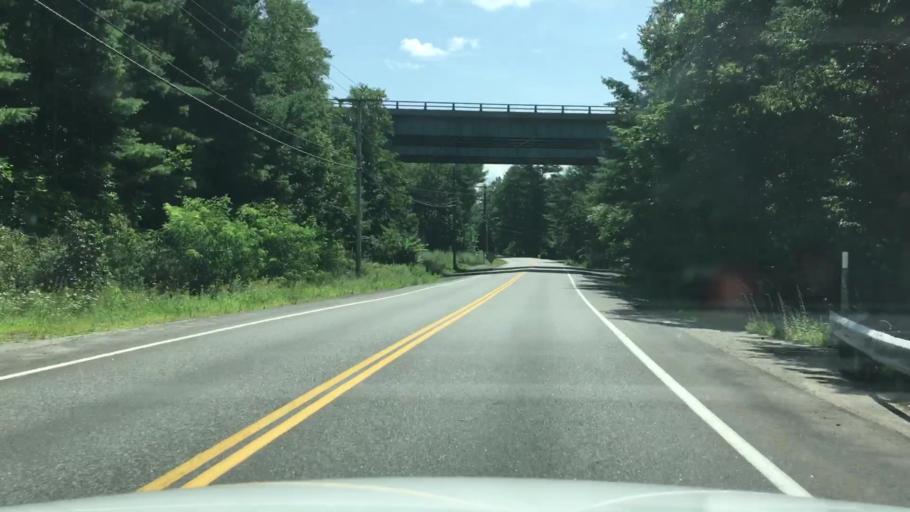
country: US
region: Maine
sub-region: Kennebec County
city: Augusta
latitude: 44.3387
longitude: -69.8082
